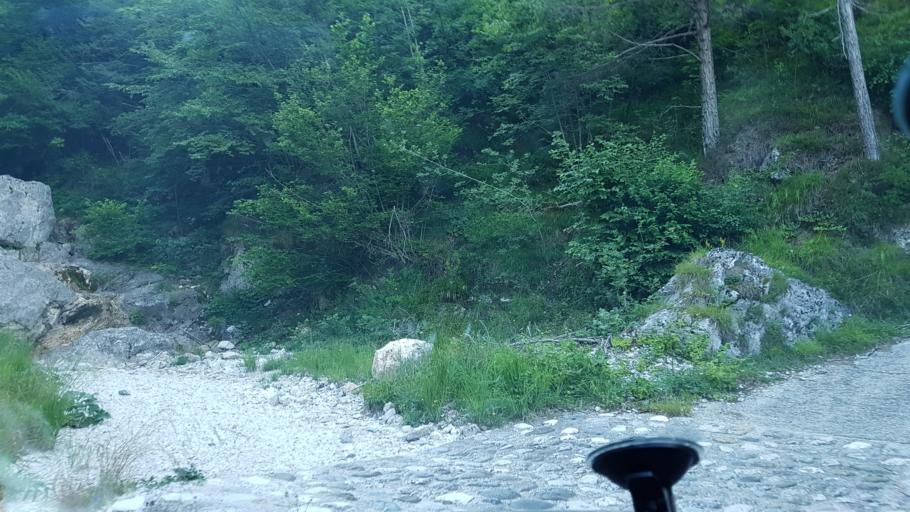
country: IT
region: Friuli Venezia Giulia
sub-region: Provincia di Udine
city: Dogna
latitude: 46.4418
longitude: 13.2972
